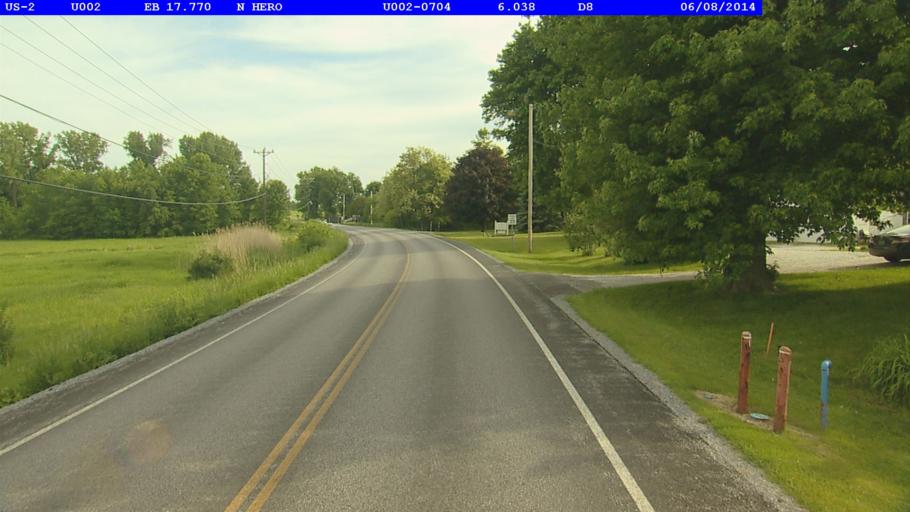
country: US
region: Vermont
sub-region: Grand Isle County
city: North Hero
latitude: 44.8124
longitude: -73.2920
